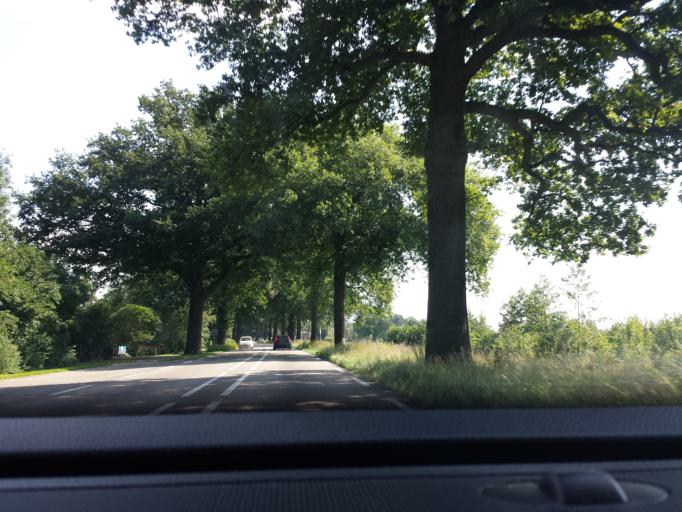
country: NL
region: Gelderland
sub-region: Gemeente Lochem
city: Lochem
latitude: 52.1645
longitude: 6.4359
